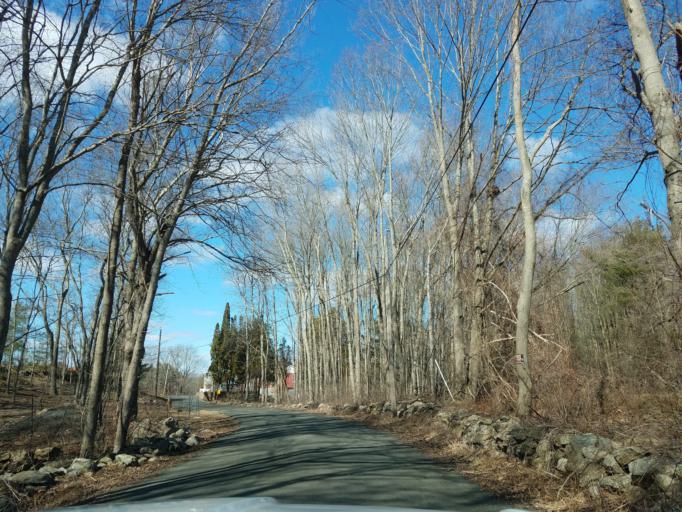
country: US
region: Connecticut
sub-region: Windham County
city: North Grosvenor Dale
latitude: 41.9958
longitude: -71.8843
